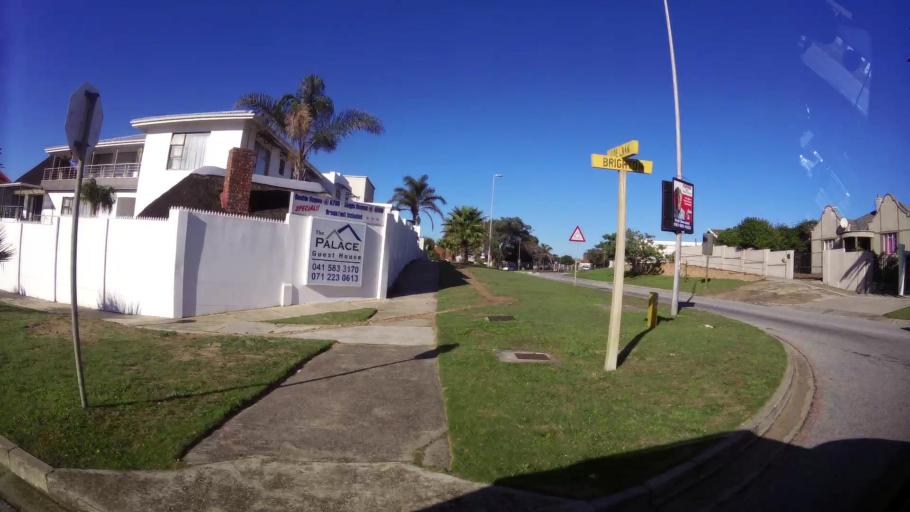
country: ZA
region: Eastern Cape
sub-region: Nelson Mandela Bay Metropolitan Municipality
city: Port Elizabeth
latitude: -33.9841
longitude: 25.6613
